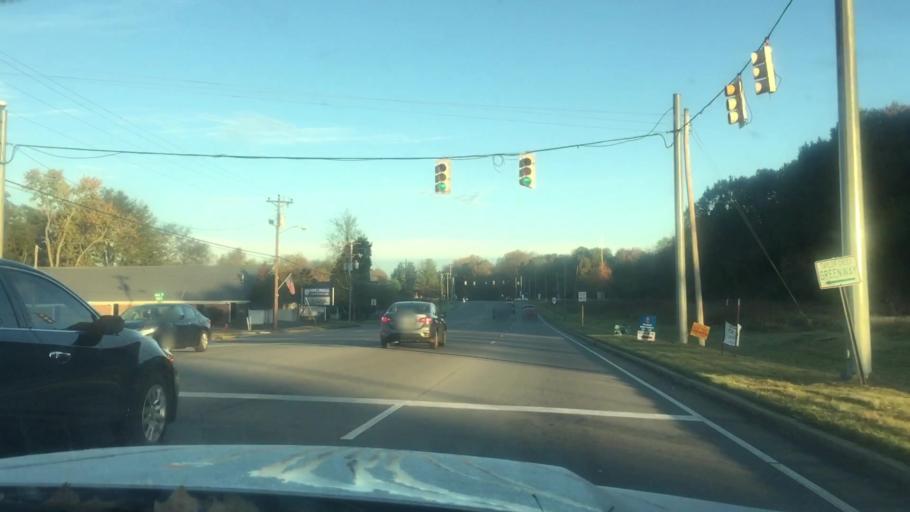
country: US
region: Tennessee
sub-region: Franklin County
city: Estill Springs
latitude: 35.2710
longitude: -86.1282
